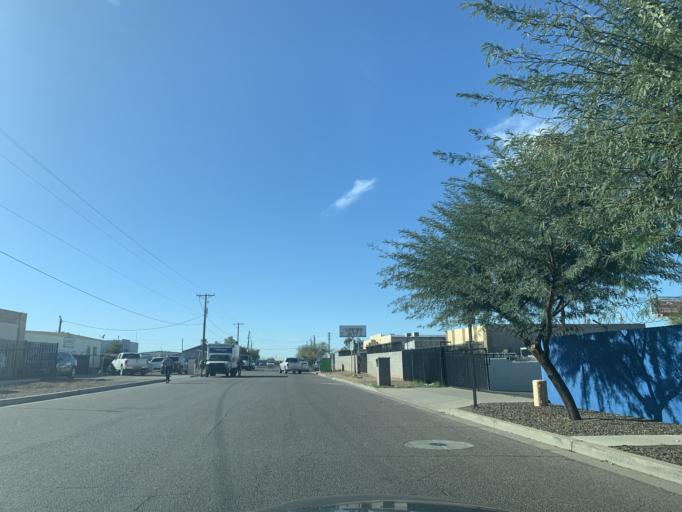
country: US
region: Arizona
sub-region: Maricopa County
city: Tempe Junction
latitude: 33.4210
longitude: -111.9931
